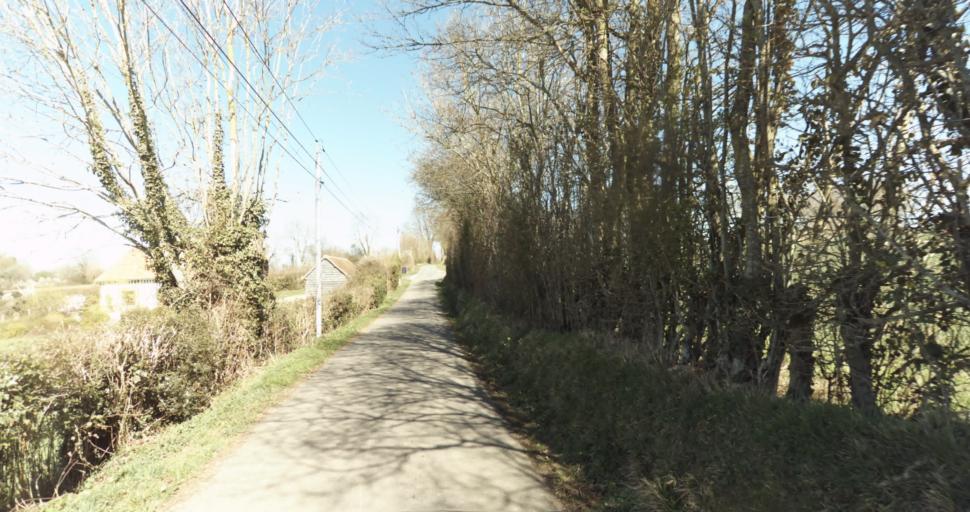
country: FR
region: Lower Normandy
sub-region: Departement du Calvados
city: Livarot
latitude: 48.9914
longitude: 0.1028
